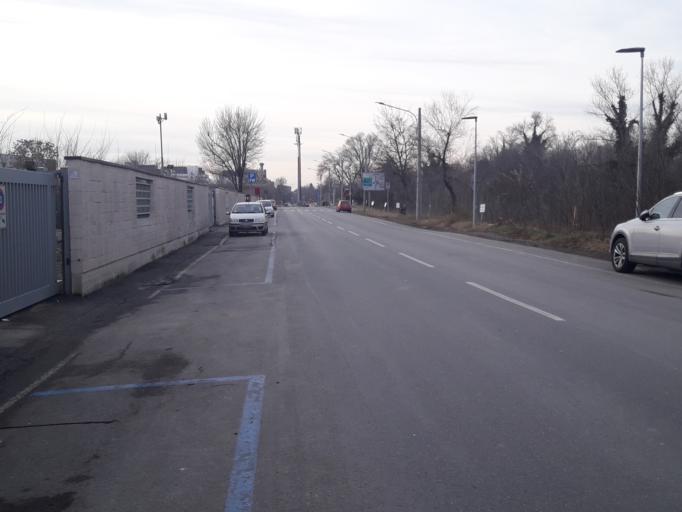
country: IT
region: Emilia-Romagna
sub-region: Provincia di Bologna
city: Bologna
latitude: 44.5071
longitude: 11.3135
